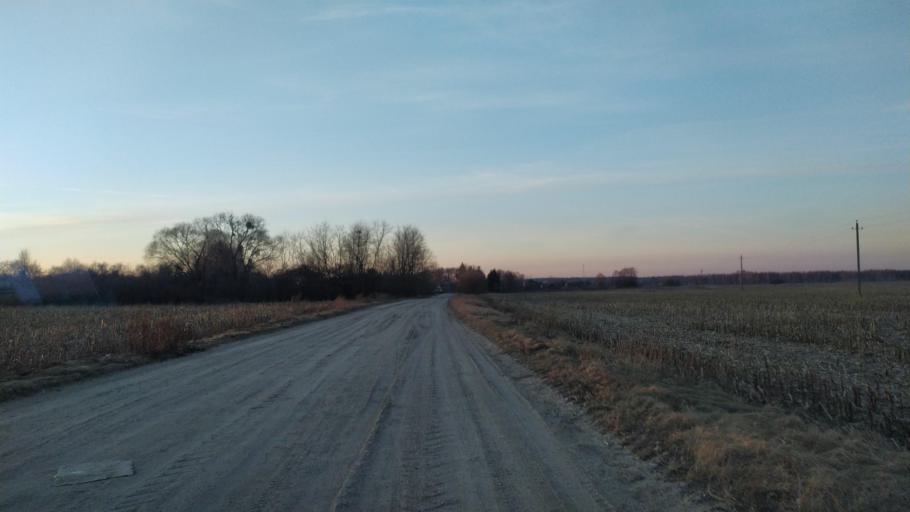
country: BY
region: Brest
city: Pruzhany
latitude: 52.5496
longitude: 24.2333
